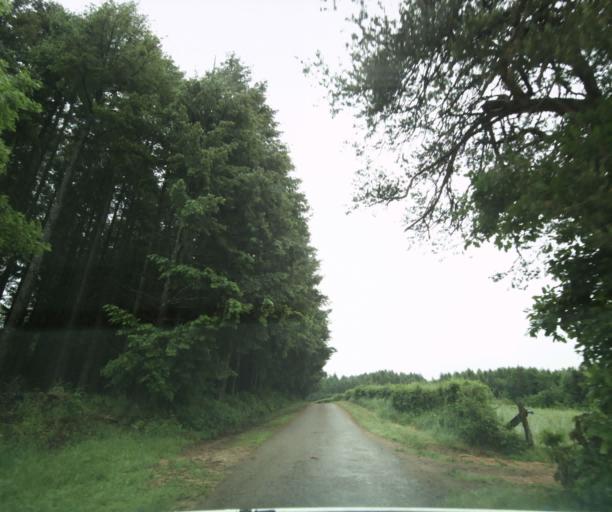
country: FR
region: Bourgogne
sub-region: Departement de Saone-et-Loire
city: Charolles
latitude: 46.4549
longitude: 4.4096
